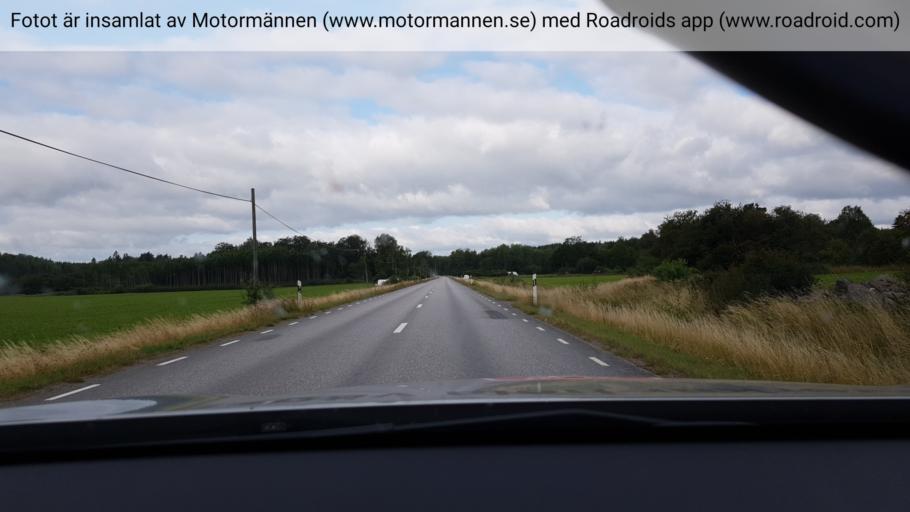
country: SE
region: Stockholm
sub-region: Norrtalje Kommun
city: Skanninge
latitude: 59.8953
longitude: 18.4370
